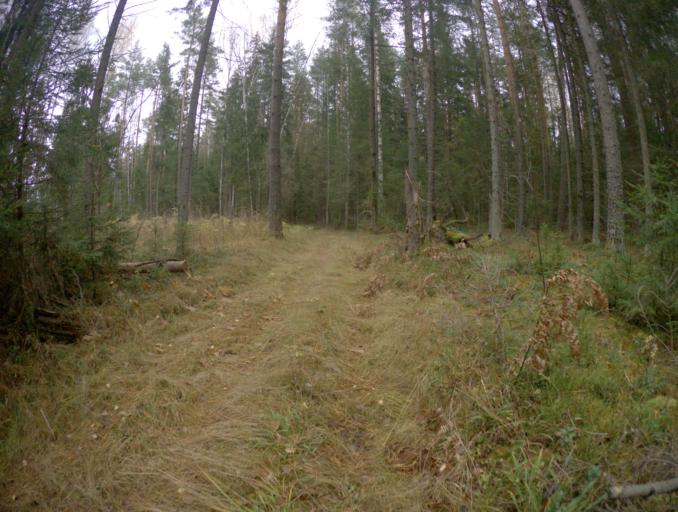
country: RU
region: Vladimir
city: Orgtrud
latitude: 56.1090
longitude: 40.6083
